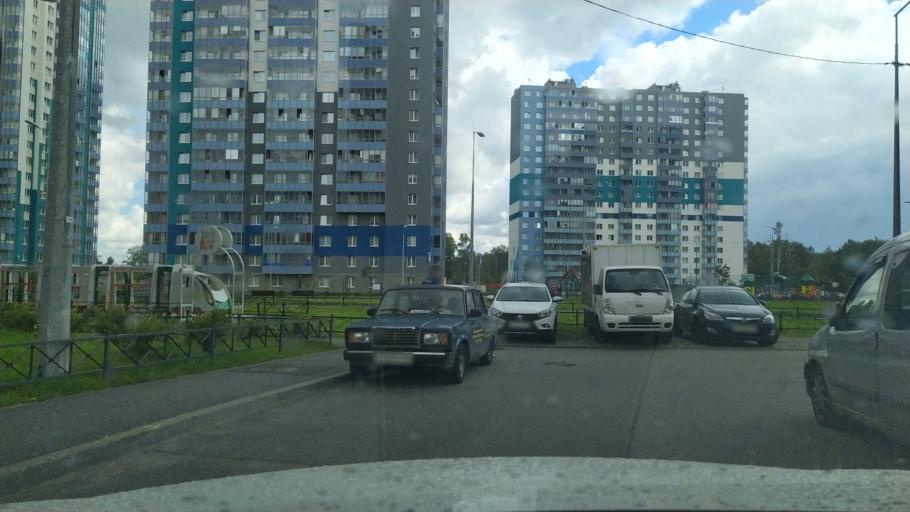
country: RU
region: Leningrad
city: Murino
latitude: 60.0288
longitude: 30.4559
